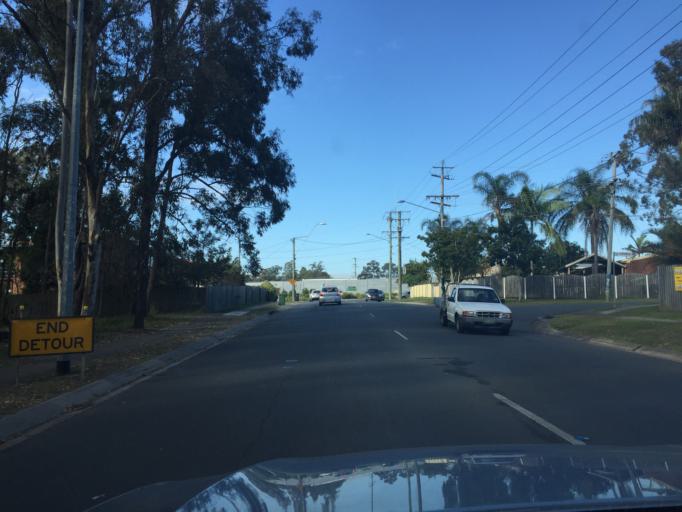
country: AU
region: Queensland
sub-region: Logan
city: Slacks Creek
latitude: -27.6461
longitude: 153.1531
